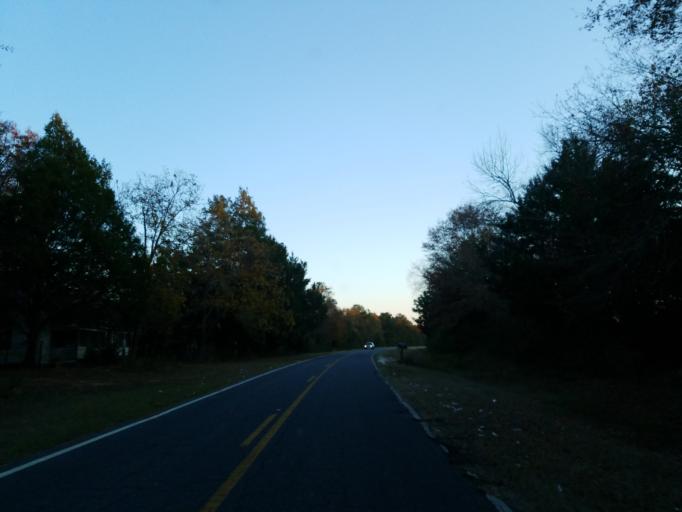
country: US
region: Georgia
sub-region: Ben Hill County
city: Fitzgerald
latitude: 31.6628
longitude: -83.3923
